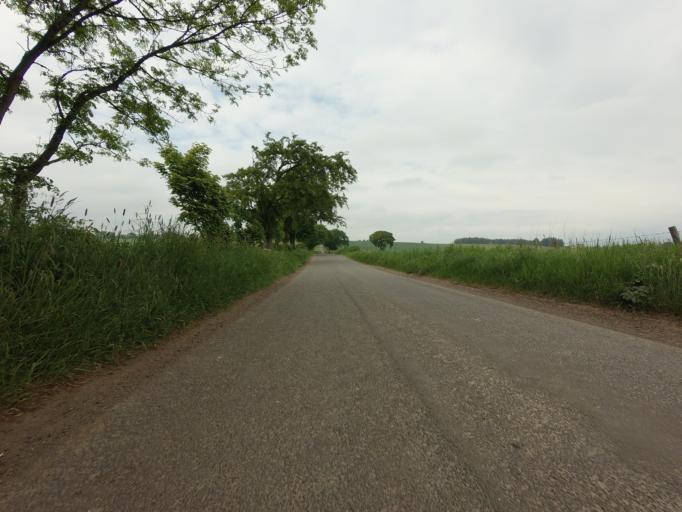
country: GB
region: Scotland
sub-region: Perth and Kinross
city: Kinross
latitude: 56.1759
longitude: -3.4389
